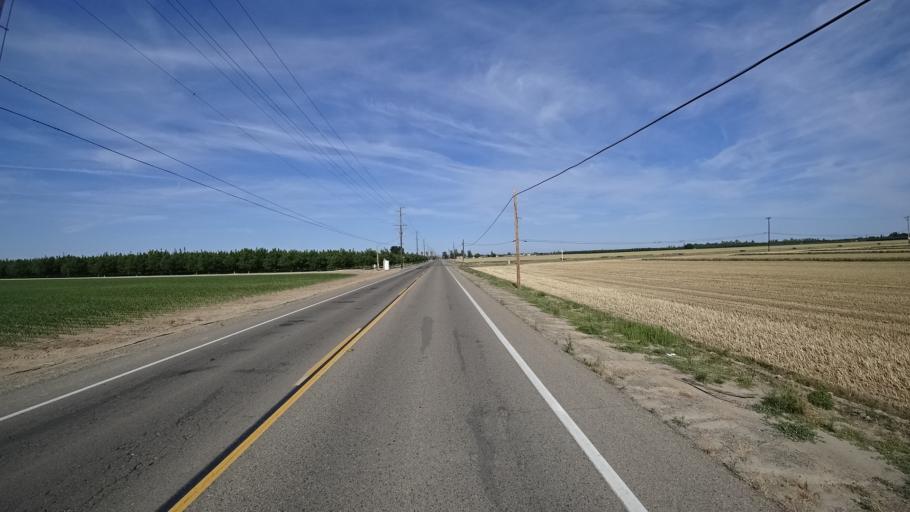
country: US
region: California
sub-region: Kings County
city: Hanford
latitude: 36.3425
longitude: -119.6088
